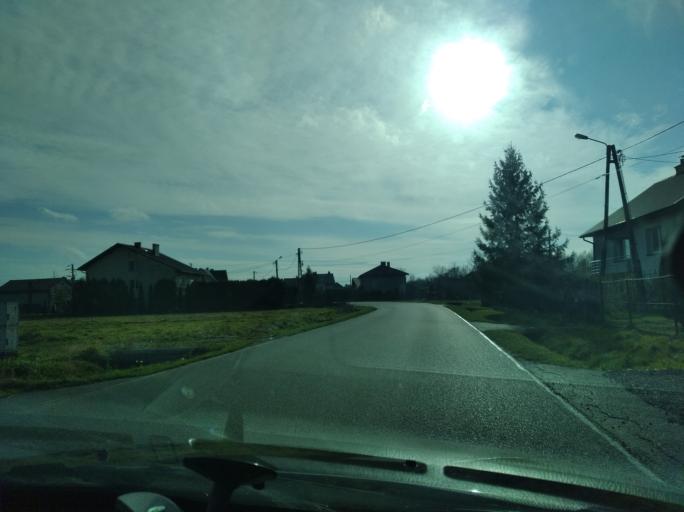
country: PL
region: Subcarpathian Voivodeship
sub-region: Powiat ropczycko-sedziszowski
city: Sedziszow Malopolski
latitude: 50.0808
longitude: 21.7507
